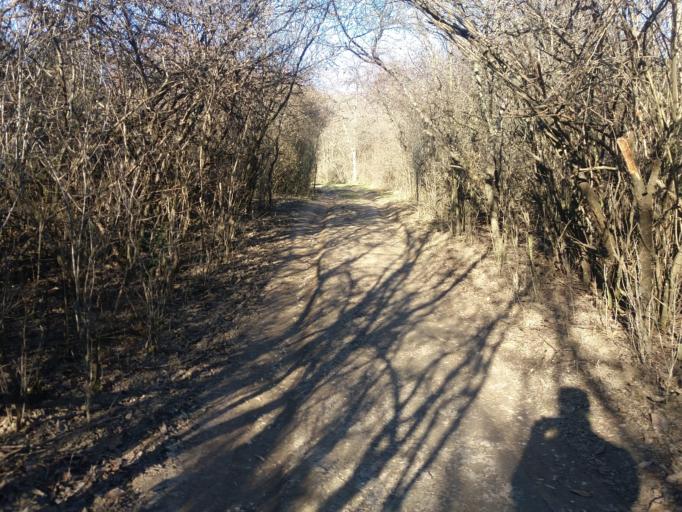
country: HU
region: Pest
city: Budaors
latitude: 47.4709
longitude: 18.9490
